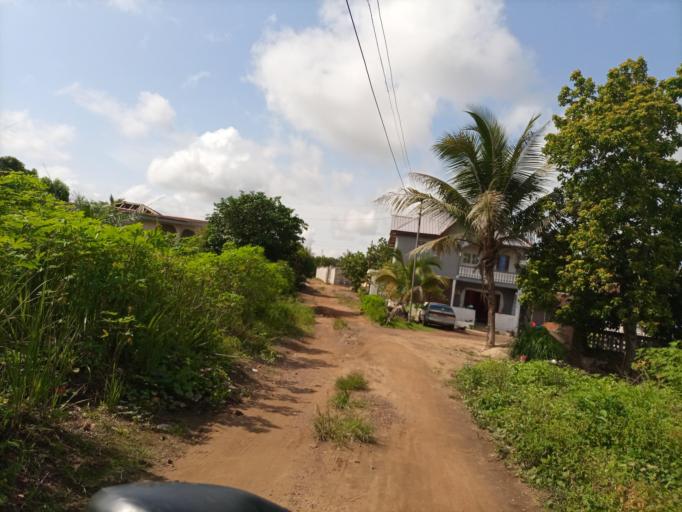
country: SL
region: Southern Province
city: Bo
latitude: 7.9681
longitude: -11.7640
